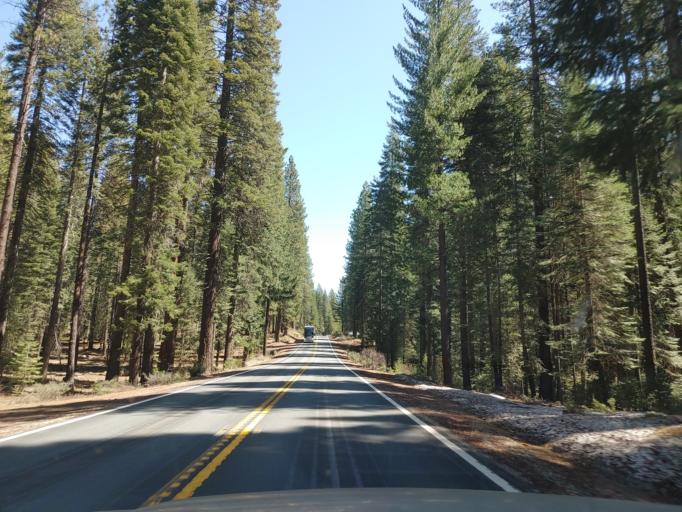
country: US
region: California
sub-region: Siskiyou County
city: McCloud
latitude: 41.2672
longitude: -121.9184
